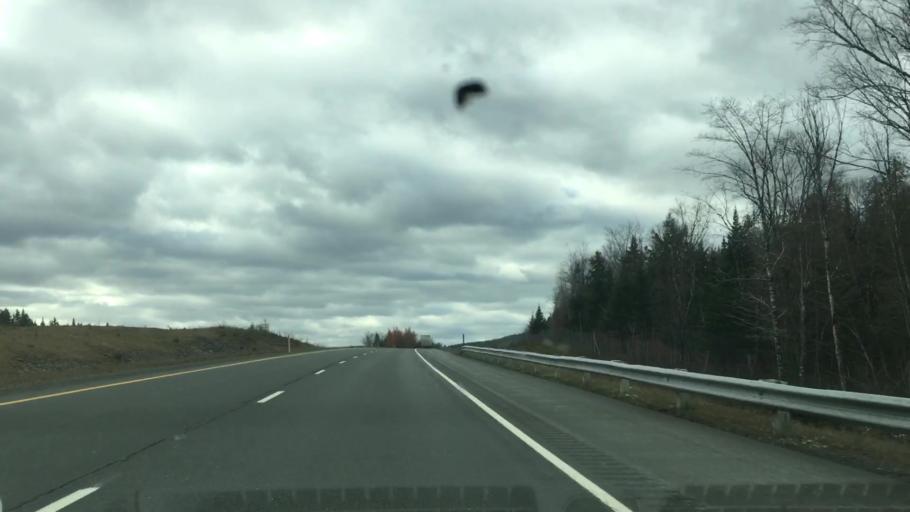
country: US
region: Maine
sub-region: Aroostook County
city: Fort Fairfield
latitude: 46.6595
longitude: -67.7334
